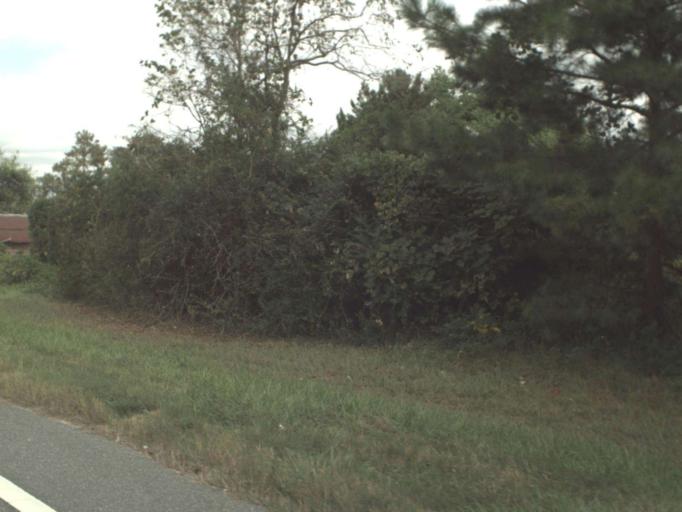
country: US
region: Florida
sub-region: Calhoun County
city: Blountstown
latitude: 30.4353
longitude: -85.1891
